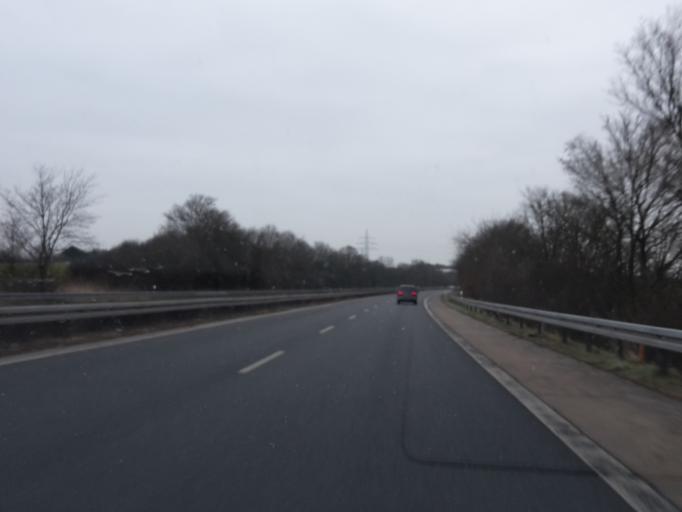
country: DE
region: Hesse
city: Liederbach
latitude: 50.1399
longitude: 8.4823
